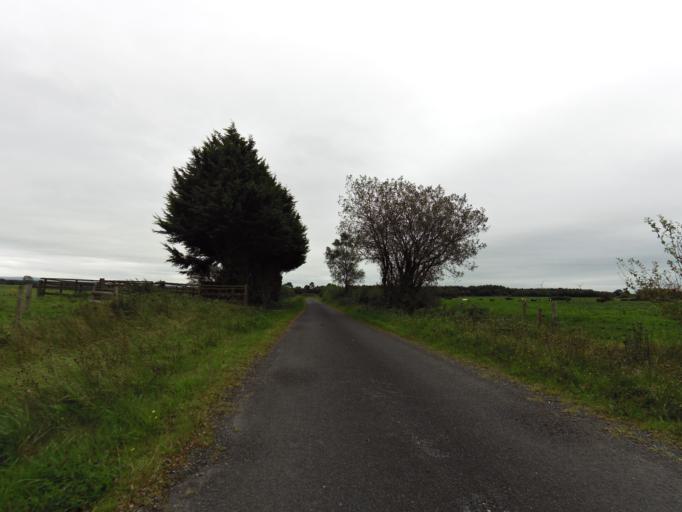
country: IE
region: Leinster
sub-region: Uibh Fhaili
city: Ferbane
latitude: 53.2511
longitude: -7.7380
